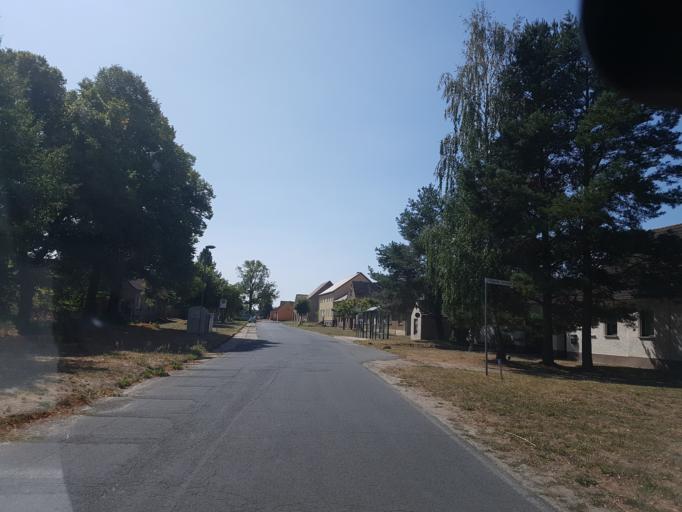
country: DE
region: Saxony-Anhalt
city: Kropstadt
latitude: 52.0317
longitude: 12.7609
